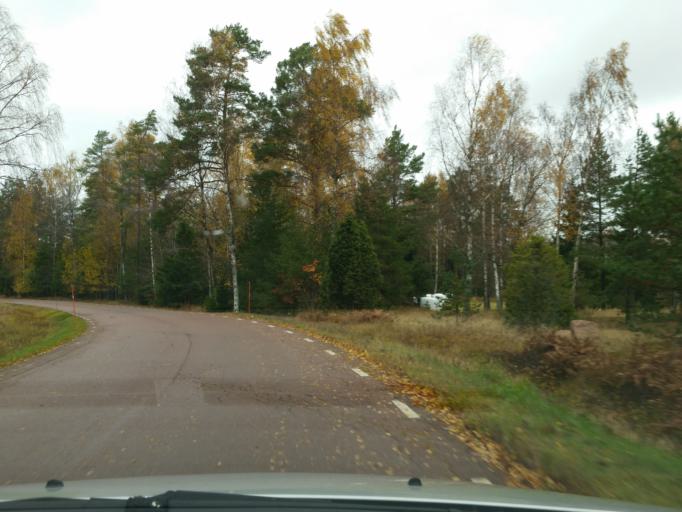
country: AX
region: Alands landsbygd
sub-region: Lumparland
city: Lumparland
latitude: 60.1300
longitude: 20.2709
